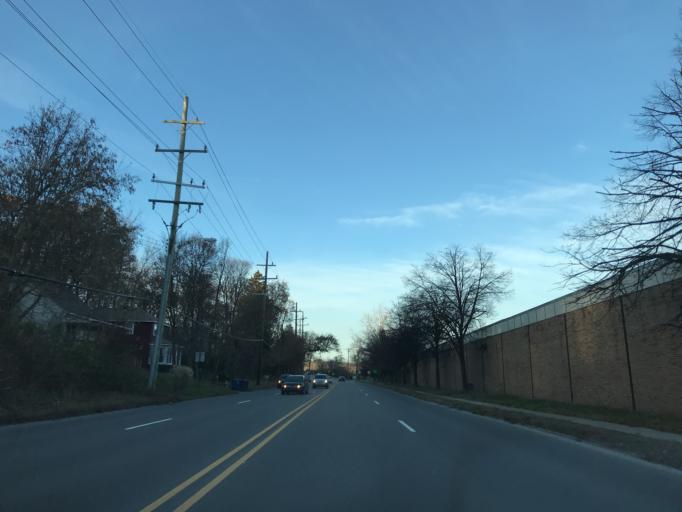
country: US
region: Michigan
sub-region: Washtenaw County
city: Ann Arbor
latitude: 42.2954
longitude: -83.7467
